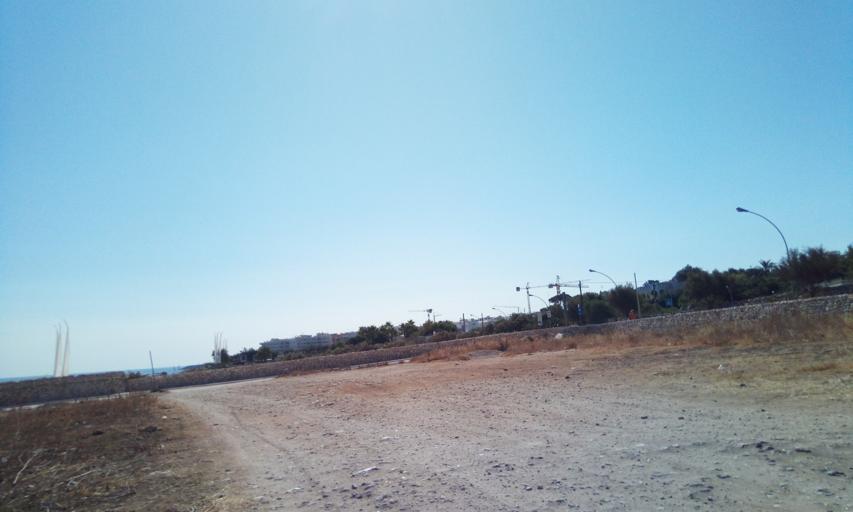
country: IT
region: Apulia
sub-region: Provincia di Bari
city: Polignano a Mare
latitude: 40.9999
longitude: 17.2088
